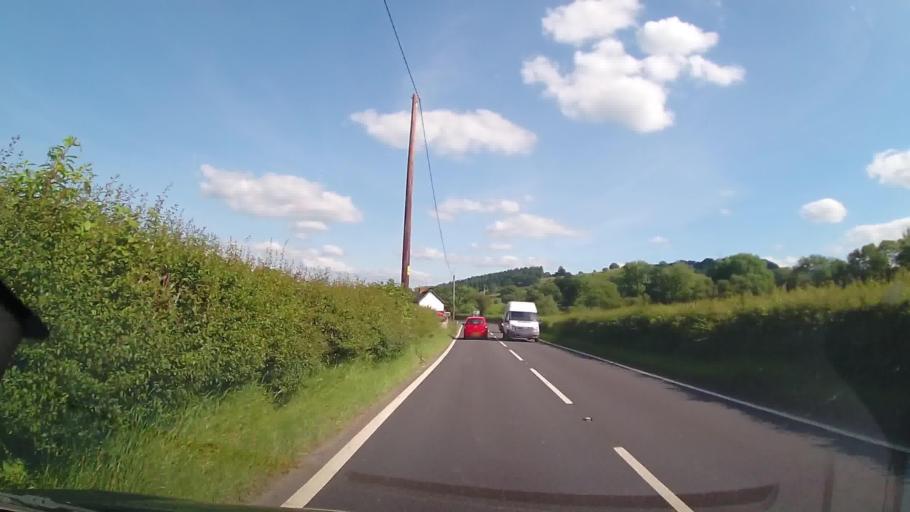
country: GB
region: Wales
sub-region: Sir Powys
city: Llanfyllin
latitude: 52.6632
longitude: -3.2810
